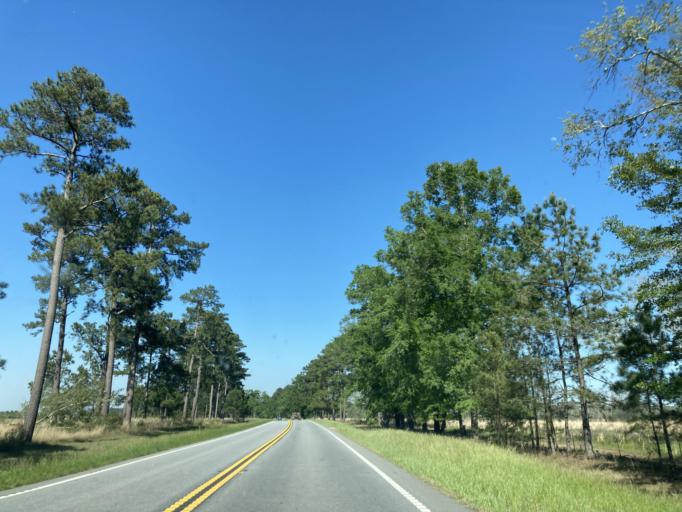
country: US
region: Georgia
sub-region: Baker County
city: Newton
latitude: 31.3369
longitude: -84.3164
